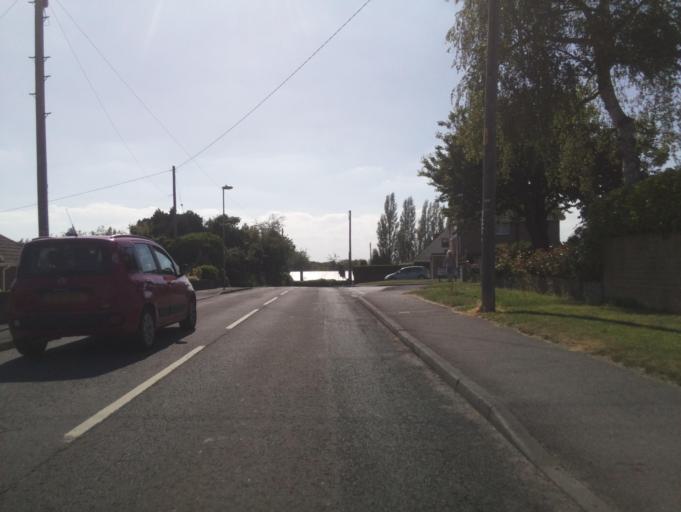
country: GB
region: England
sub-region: Hampshire
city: Andover
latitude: 51.2211
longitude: -1.5024
